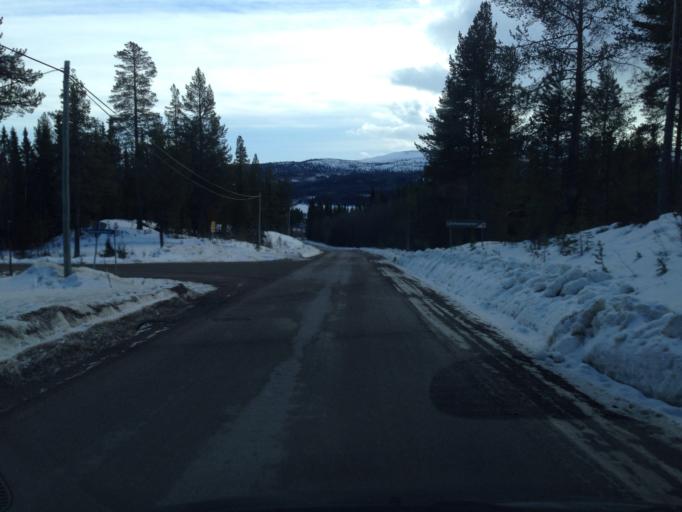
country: SE
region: Jaemtland
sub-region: Harjedalens Kommun
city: Sveg
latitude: 62.1237
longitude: 13.2654
